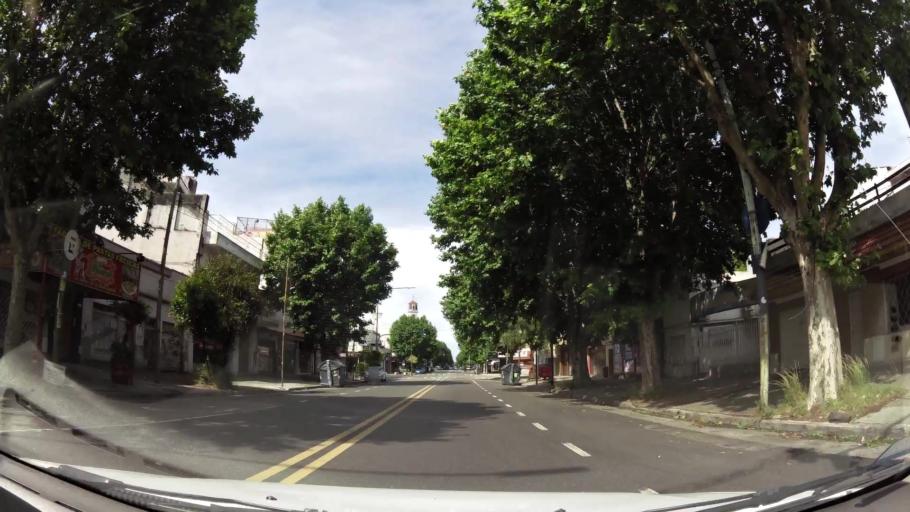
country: AR
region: Buenos Aires F.D.
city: Villa Lugano
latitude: -34.6513
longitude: -58.5142
